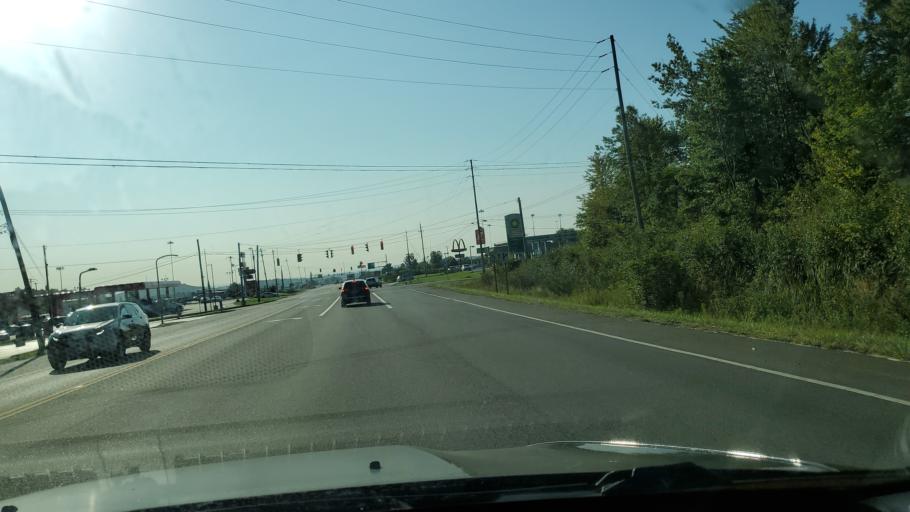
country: US
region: Ohio
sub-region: Trumbull County
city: McDonald
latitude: 41.1445
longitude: -80.7237
